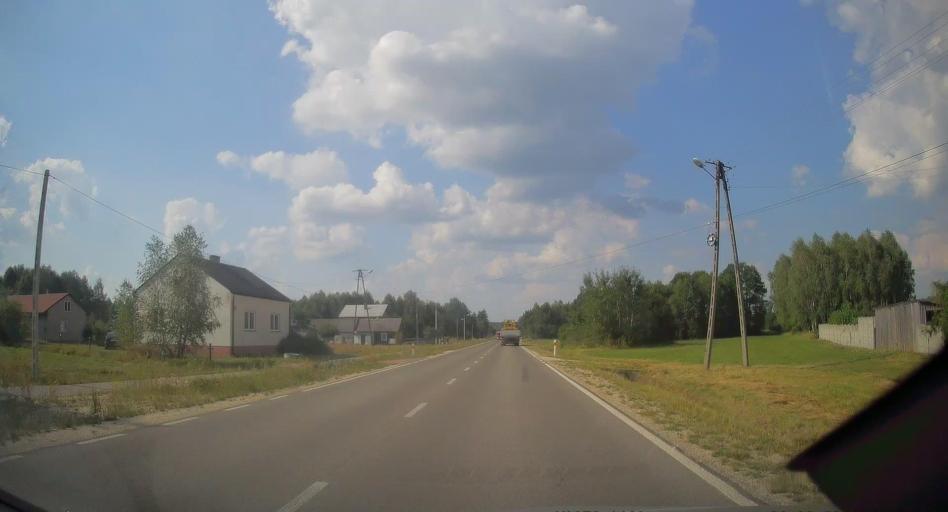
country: PL
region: Swietokrzyskie
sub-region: Powiat konecki
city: Radoszyce
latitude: 51.0558
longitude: 20.2791
